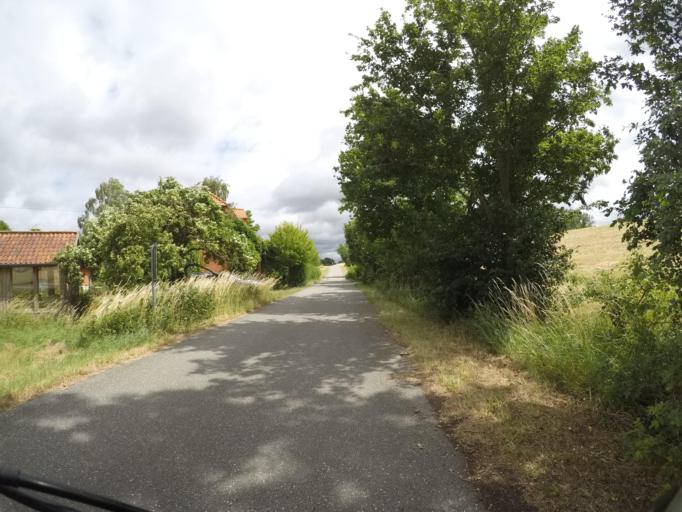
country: DE
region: Lower Saxony
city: Dannenberg
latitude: 53.1471
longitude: 11.0970
